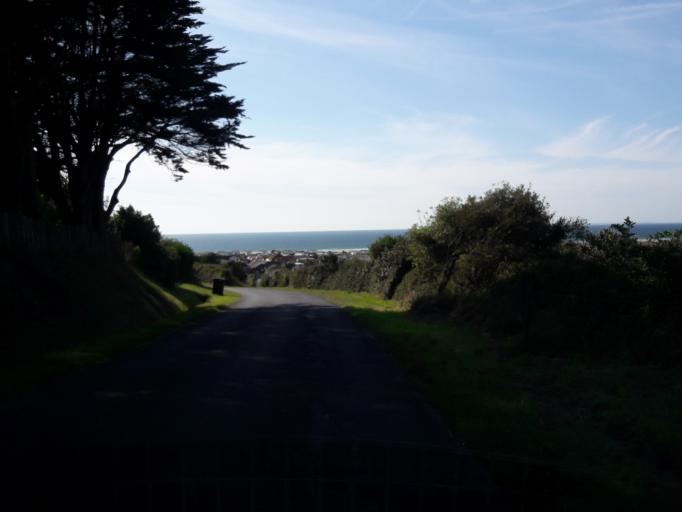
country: FR
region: Lower Normandy
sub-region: Departement de la Manche
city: Surtainville
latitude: 49.4791
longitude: -1.8378
